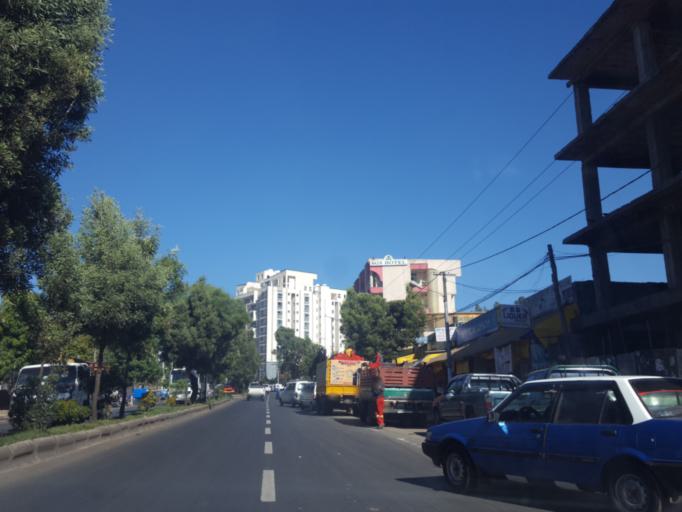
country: ET
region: Adis Abeba
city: Addis Ababa
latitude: 9.0563
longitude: 38.7409
